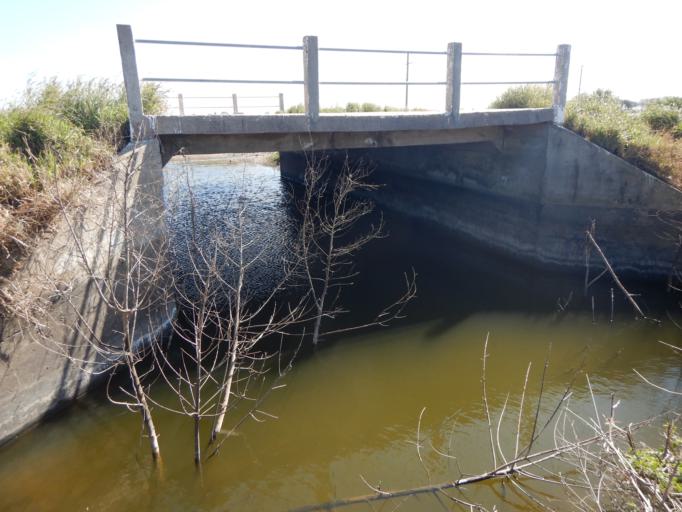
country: AR
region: Santiago del Estero
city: Los Juries
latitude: -28.6363
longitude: -61.5238
